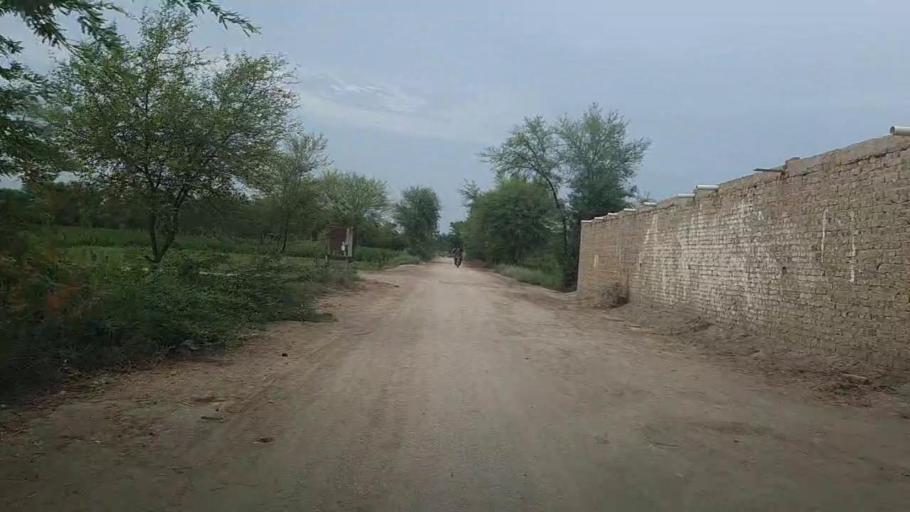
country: PK
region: Sindh
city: Karaundi
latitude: 26.9579
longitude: 68.4147
